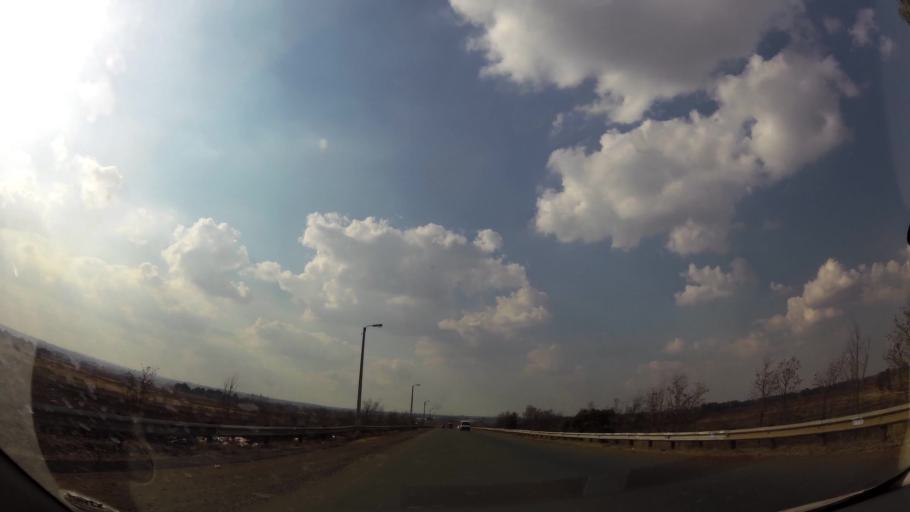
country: ZA
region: Gauteng
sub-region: Ekurhuleni Metropolitan Municipality
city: Germiston
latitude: -26.3055
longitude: 28.2089
